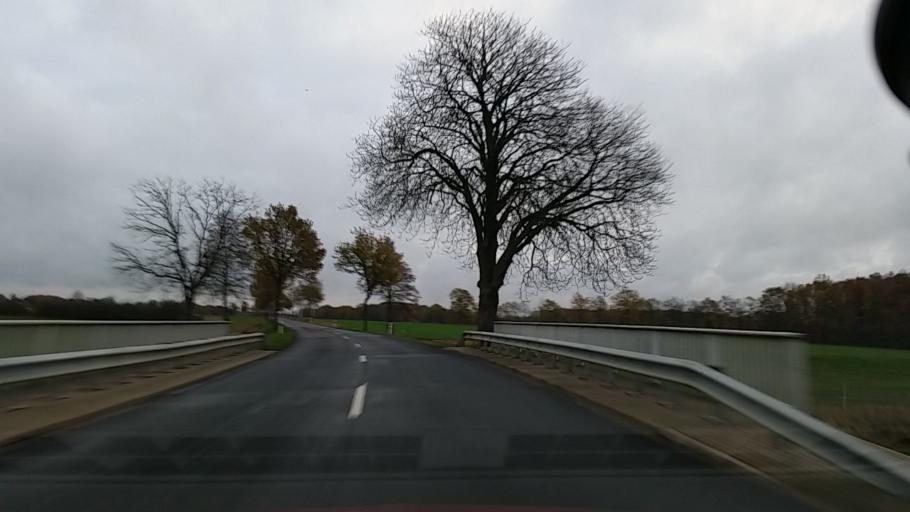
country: DE
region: Lower Saxony
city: Barwedel
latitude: 52.4999
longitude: 10.7846
